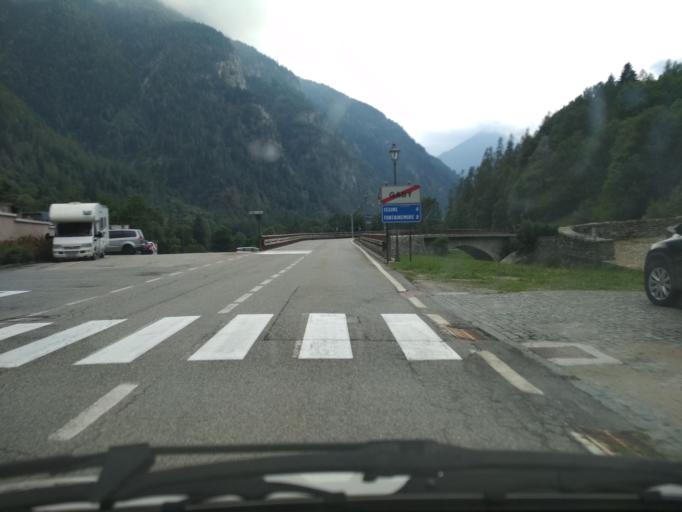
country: IT
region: Aosta Valley
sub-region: Valle d'Aosta
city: Gaby
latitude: 45.7098
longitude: 7.8811
